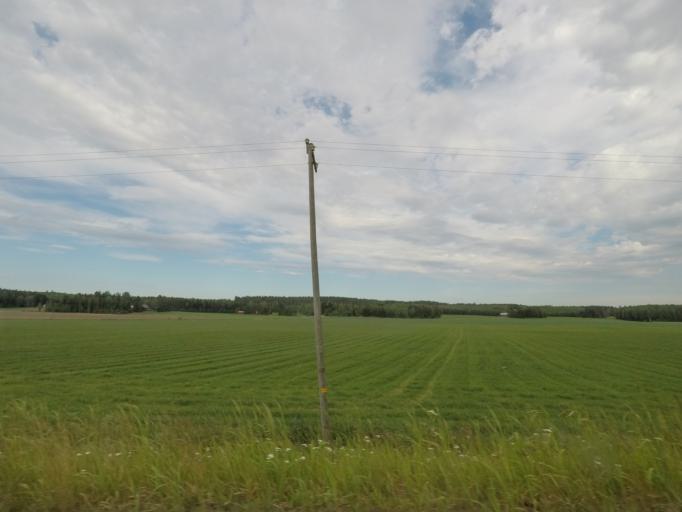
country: FI
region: Paijanne Tavastia
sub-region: Lahti
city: Hollola
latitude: 60.8557
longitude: 25.4990
